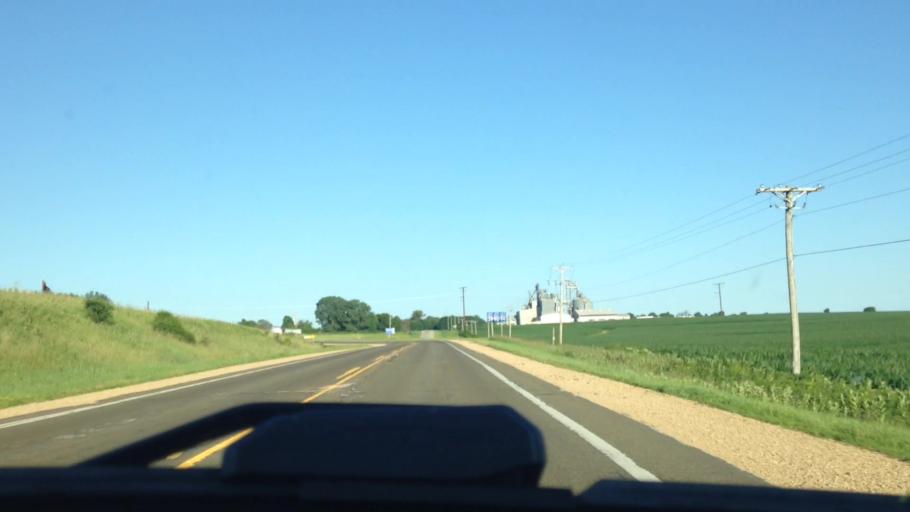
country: US
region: Wisconsin
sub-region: Columbia County
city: Poynette
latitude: 43.3377
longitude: -89.4435
